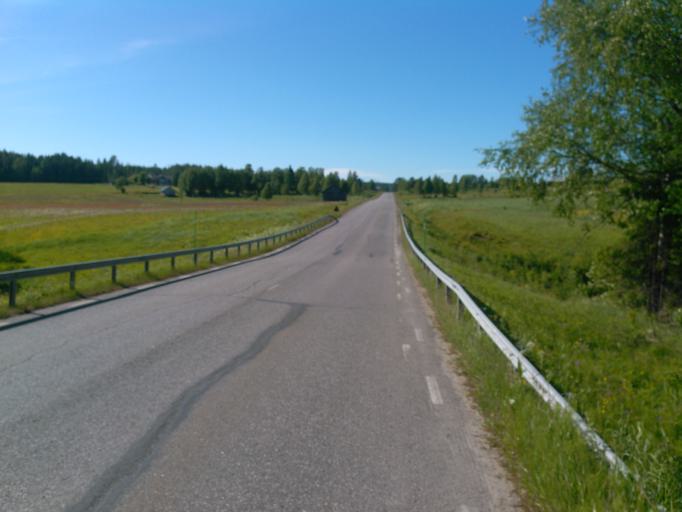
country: SE
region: Vaesterbotten
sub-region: Umea Kommun
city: Roback
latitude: 63.8237
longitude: 20.1260
